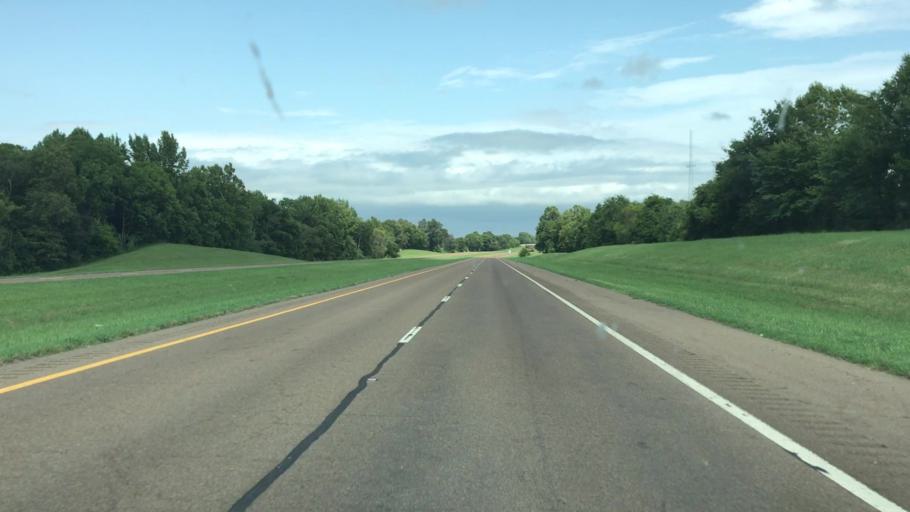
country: US
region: Tennessee
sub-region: Obion County
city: South Fulton
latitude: 36.4720
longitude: -88.9651
